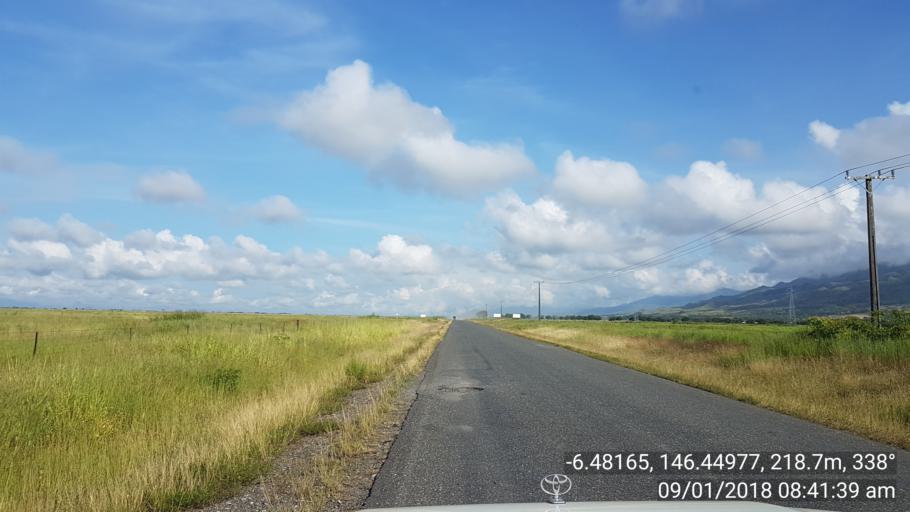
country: PG
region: Morobe
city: Lae
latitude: -6.4814
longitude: 146.4497
